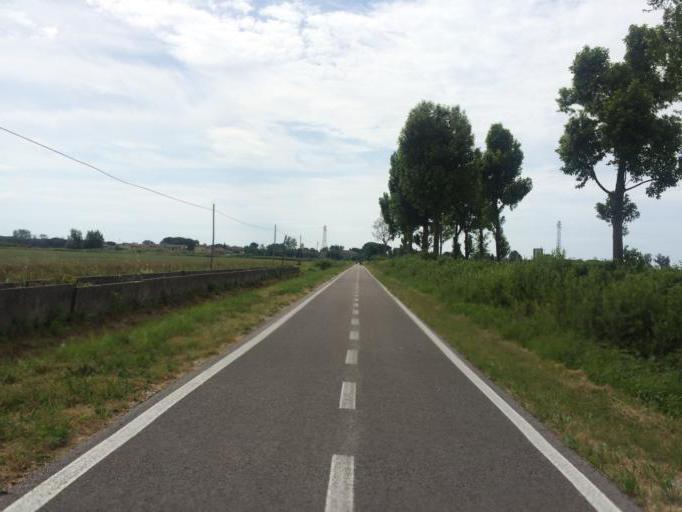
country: IT
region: Friuli Venezia Giulia
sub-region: Provincia di Udine
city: Aquileia
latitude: 45.7345
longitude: 13.3875
